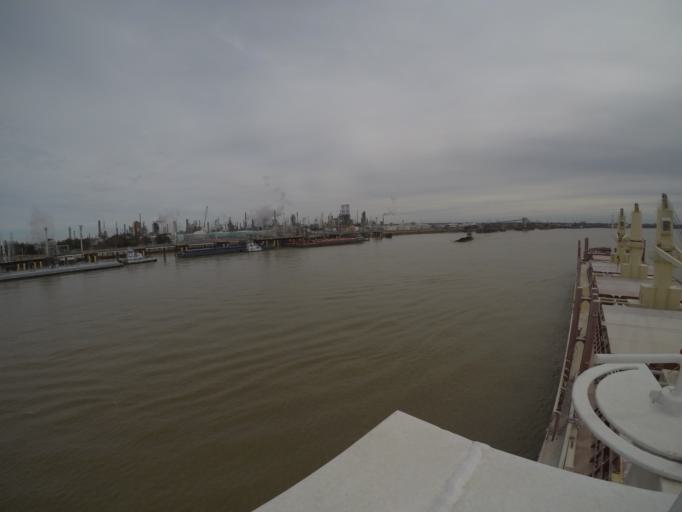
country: US
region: Louisiana
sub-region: Saint Charles Parish
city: Norco
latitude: 29.9922
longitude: -90.4116
